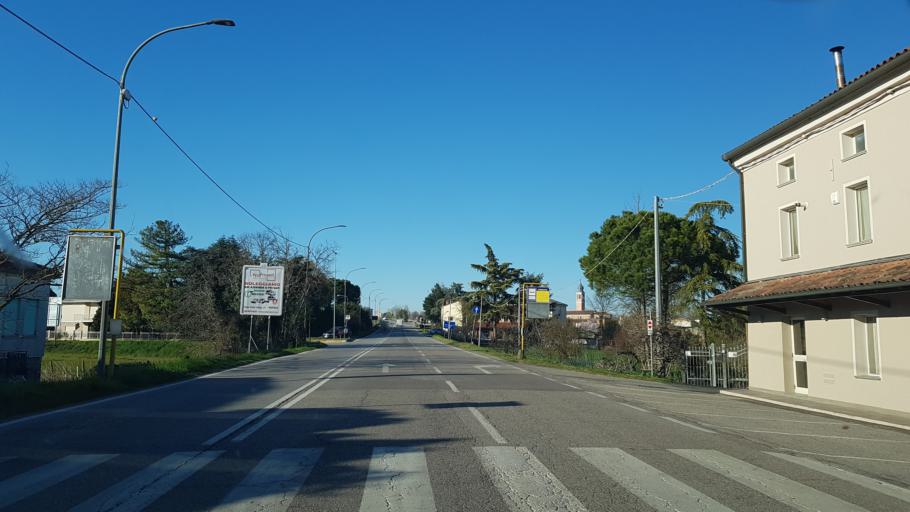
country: IT
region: Veneto
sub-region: Provincia di Padova
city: Boara Pisani
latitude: 45.1007
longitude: 11.7856
